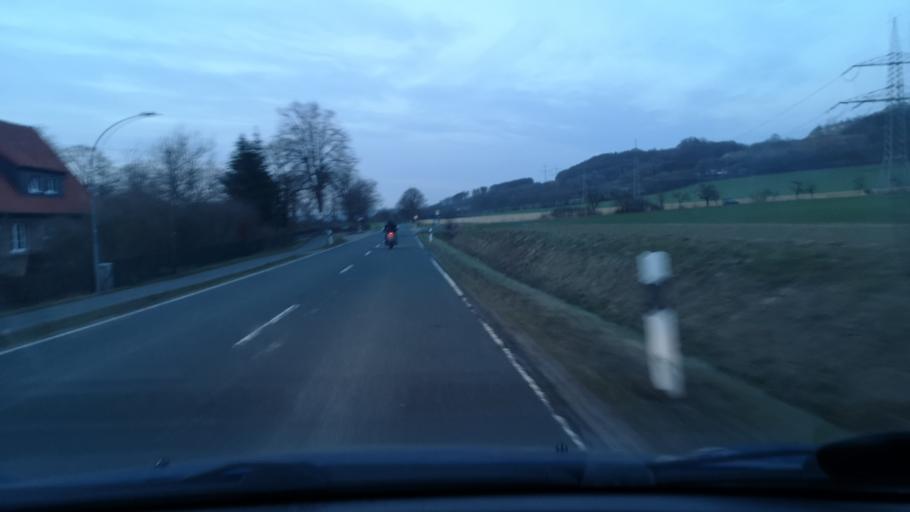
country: DE
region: Lower Saxony
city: Salzhemmendorf
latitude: 52.0487
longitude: 9.5960
